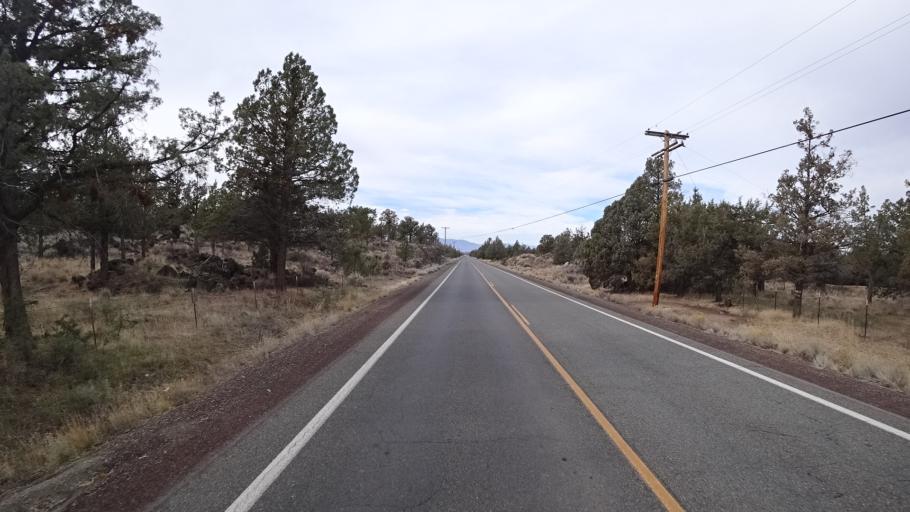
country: US
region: California
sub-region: Siskiyou County
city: Weed
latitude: 41.5929
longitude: -122.3109
